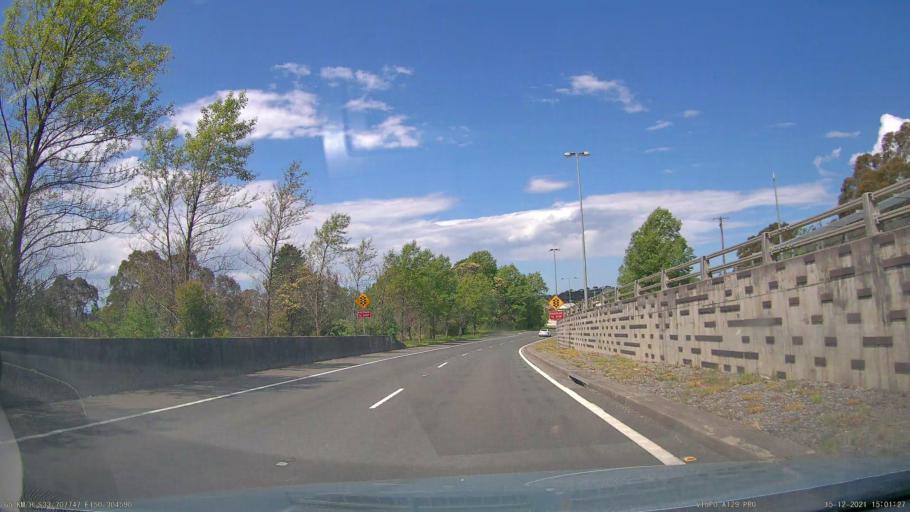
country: AU
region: New South Wales
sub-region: Blue Mountains Municipality
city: Katoomba
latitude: -33.7077
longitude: 150.3046
